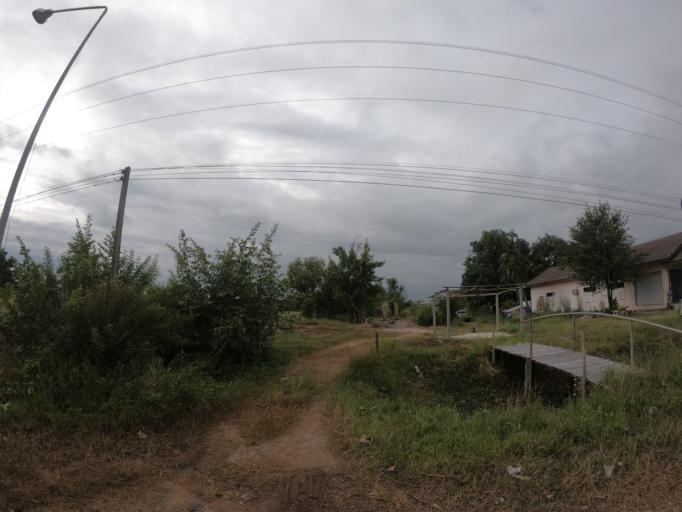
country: TH
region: Roi Et
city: Roi Et
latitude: 16.0812
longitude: 103.7034
